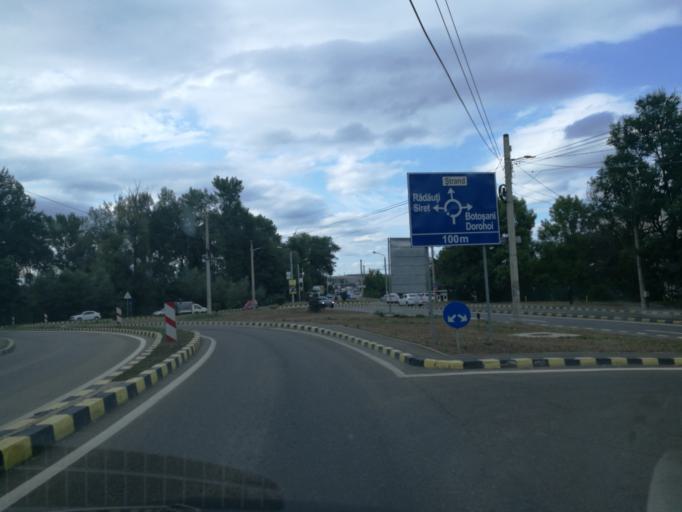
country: RO
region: Suceava
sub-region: Comuna Scheia
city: Scheia
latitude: 47.6633
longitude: 26.2476
